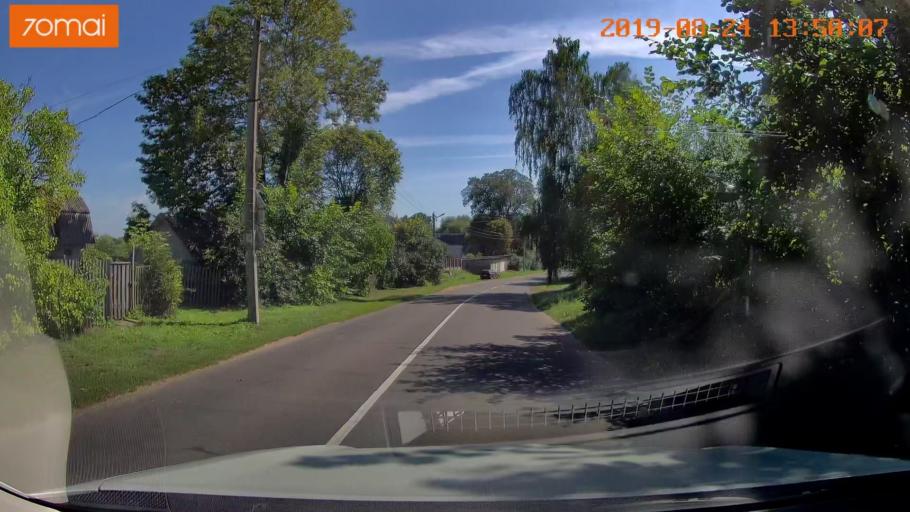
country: BY
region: Minsk
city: Samakhvalavichy
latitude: 53.6305
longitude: 27.5620
